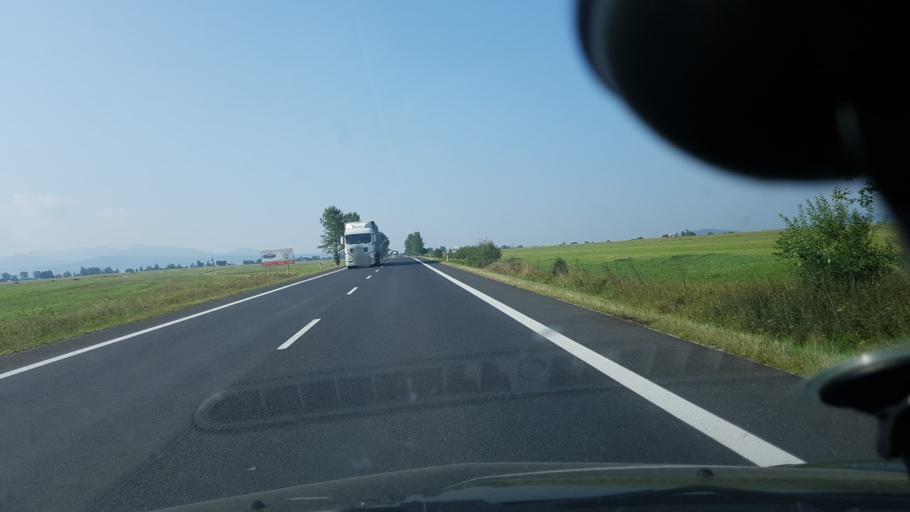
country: PL
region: Lesser Poland Voivodeship
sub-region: Powiat nowotarski
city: Chyzne
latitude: 49.4398
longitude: 19.6817
